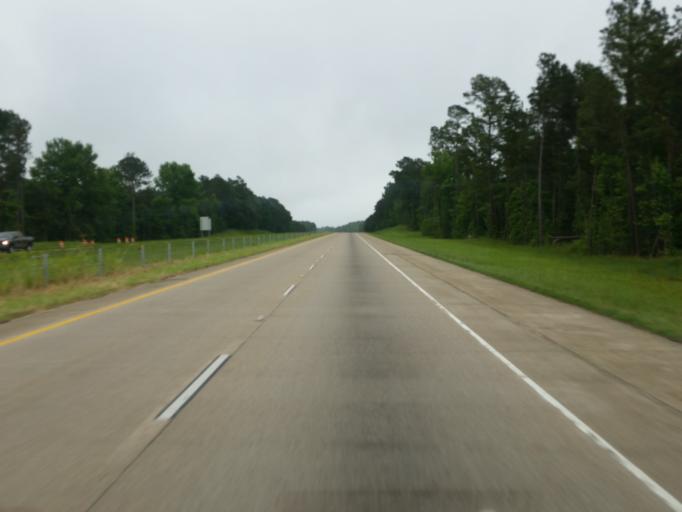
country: US
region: Louisiana
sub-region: Bienville Parish
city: Arcadia
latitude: 32.5621
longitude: -93.0385
